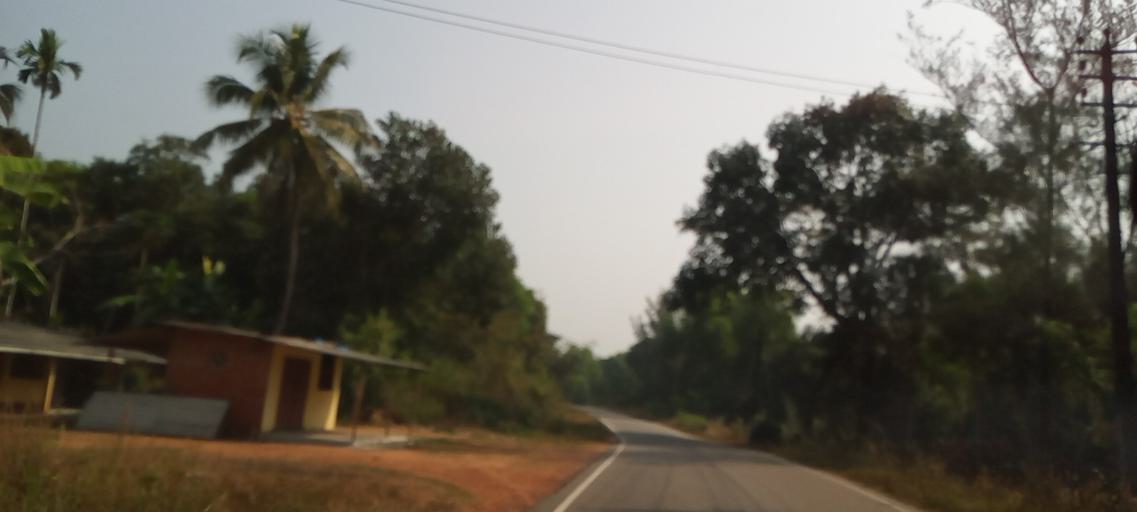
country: IN
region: Karnataka
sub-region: Udupi
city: Coondapoor
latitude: 13.5145
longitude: 74.7866
